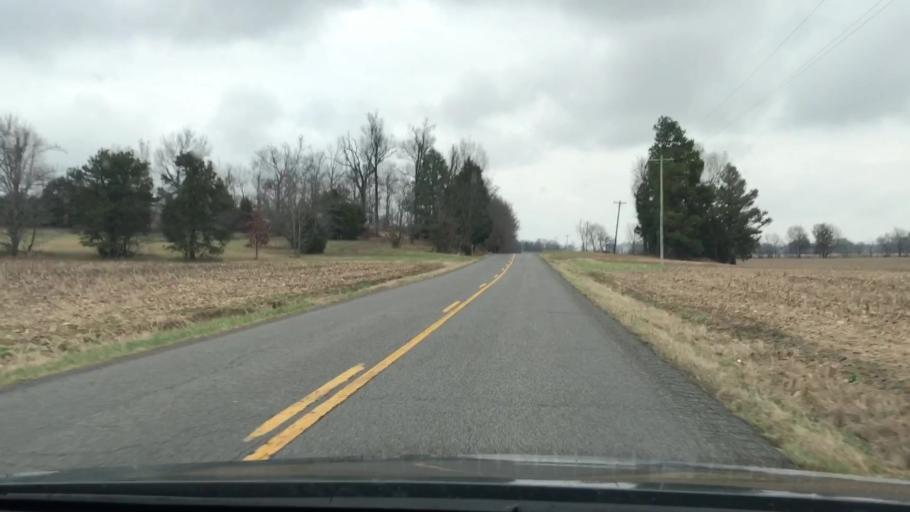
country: US
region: Kentucky
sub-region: Webster County
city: Sebree
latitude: 37.4954
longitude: -87.4492
